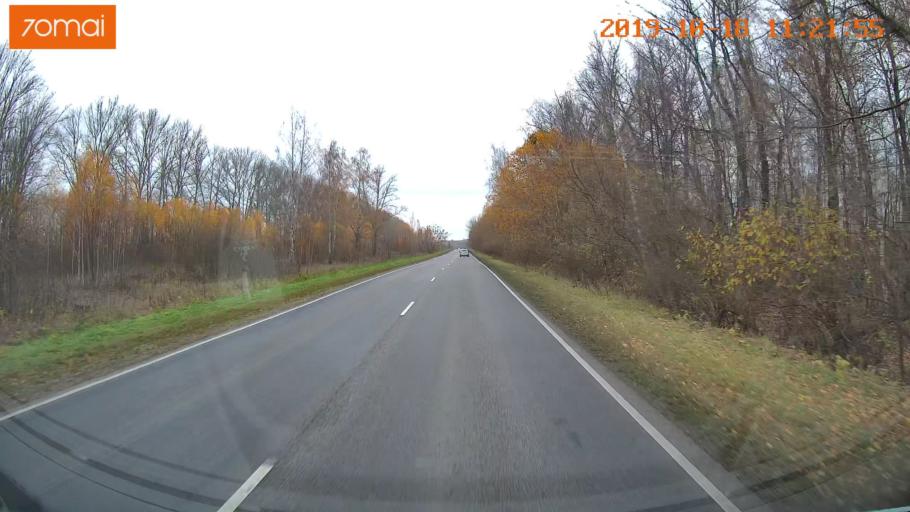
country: RU
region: Tula
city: Kimovsk
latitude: 54.0804
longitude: 38.5726
